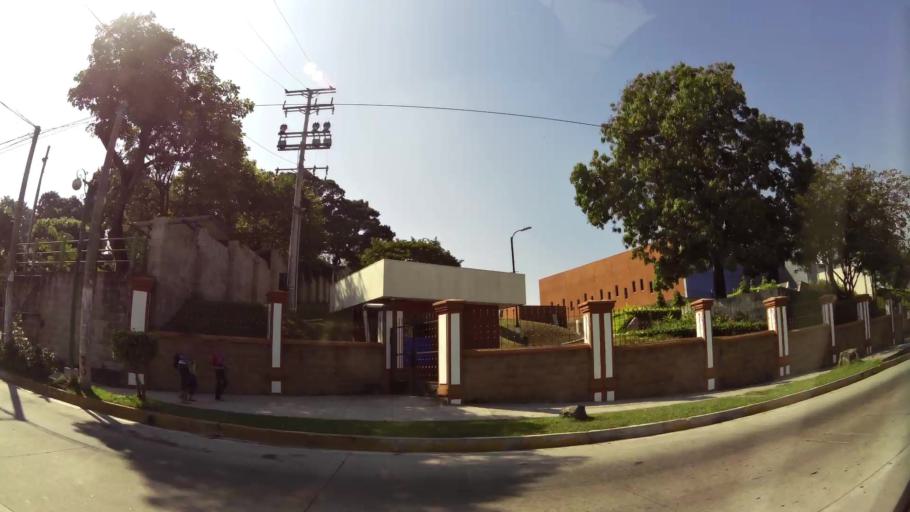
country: SV
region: La Libertad
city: Antiguo Cuscatlan
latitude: 13.6765
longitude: -89.2465
